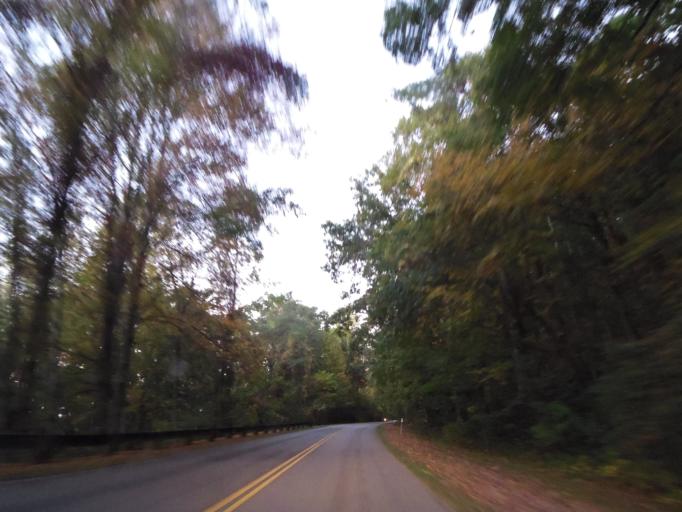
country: US
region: Tennessee
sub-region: Blount County
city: Wildwood
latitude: 35.6951
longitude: -83.8779
